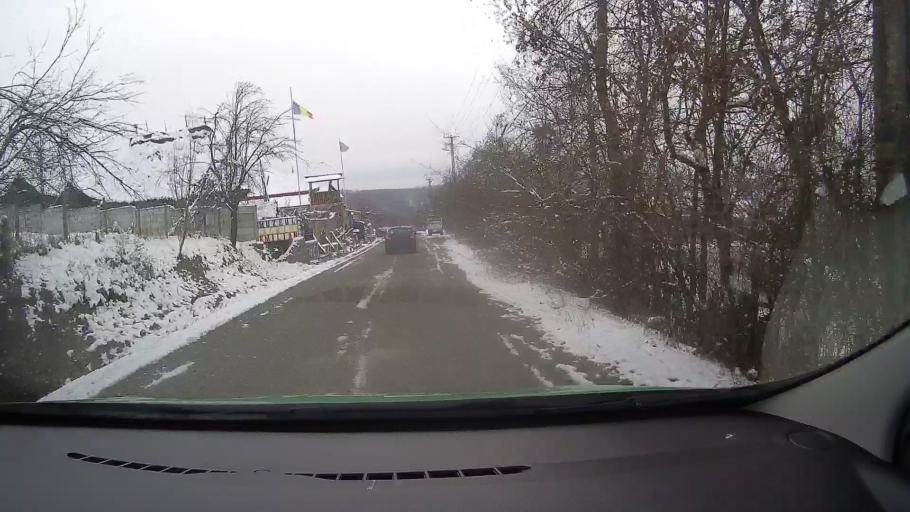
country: RO
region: Alba
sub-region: Comuna Almasu Mare
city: Almasu Mare
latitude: 46.0866
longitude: 23.1289
